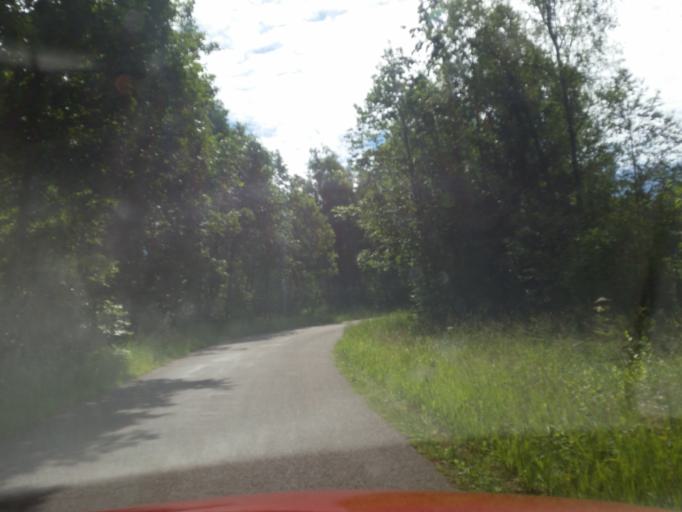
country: SE
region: Dalarna
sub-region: Gagnefs Kommun
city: Gagnef
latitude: 60.6614
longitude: 15.1213
